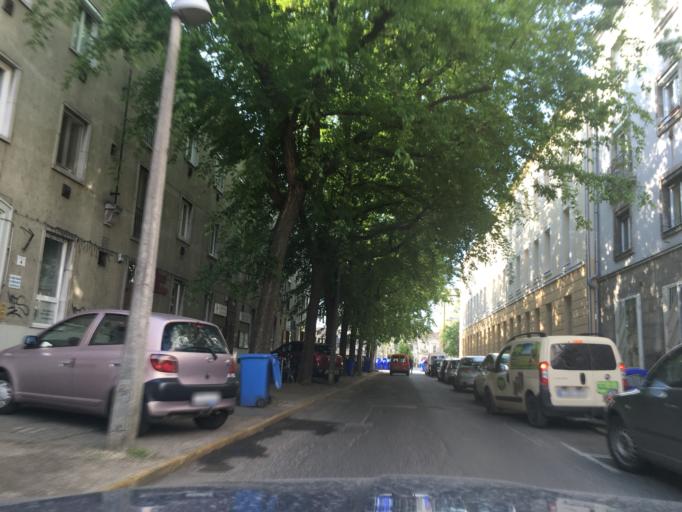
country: HU
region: Hajdu-Bihar
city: Debrecen
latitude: 47.5313
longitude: 21.6277
